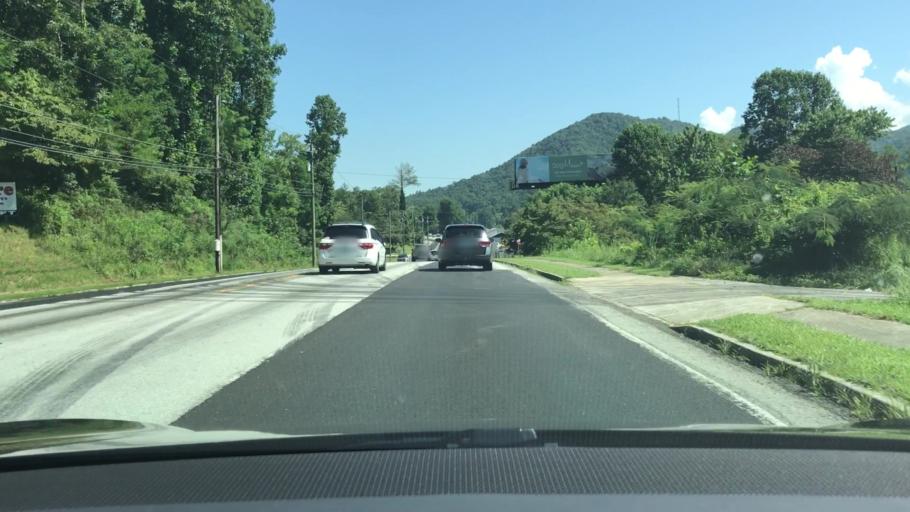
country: US
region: Georgia
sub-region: Rabun County
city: Mountain City
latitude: 34.9151
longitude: -83.3865
